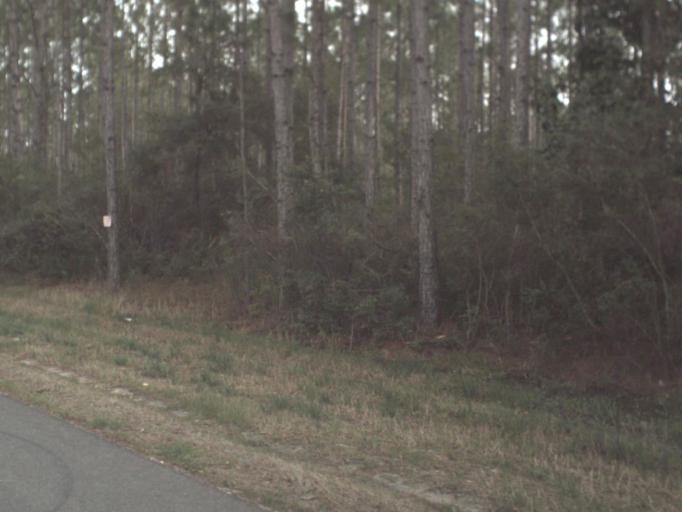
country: US
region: Florida
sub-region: Bay County
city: Callaway
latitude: 30.1526
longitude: -85.5063
